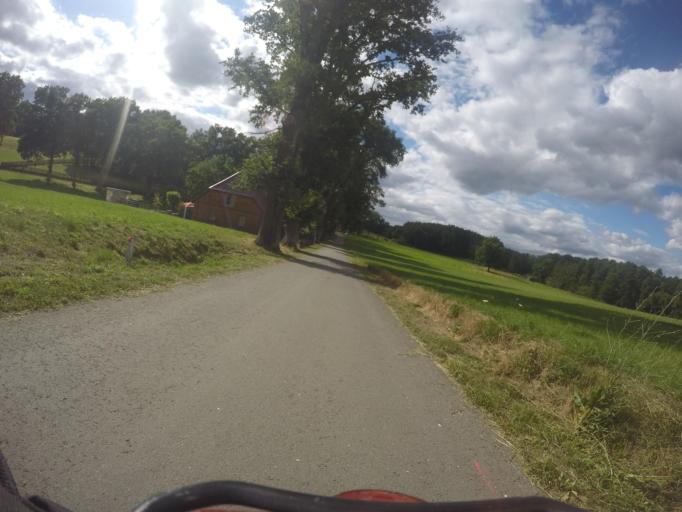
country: DE
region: Lower Saxony
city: Thomasburg
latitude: 53.2198
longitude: 10.6743
